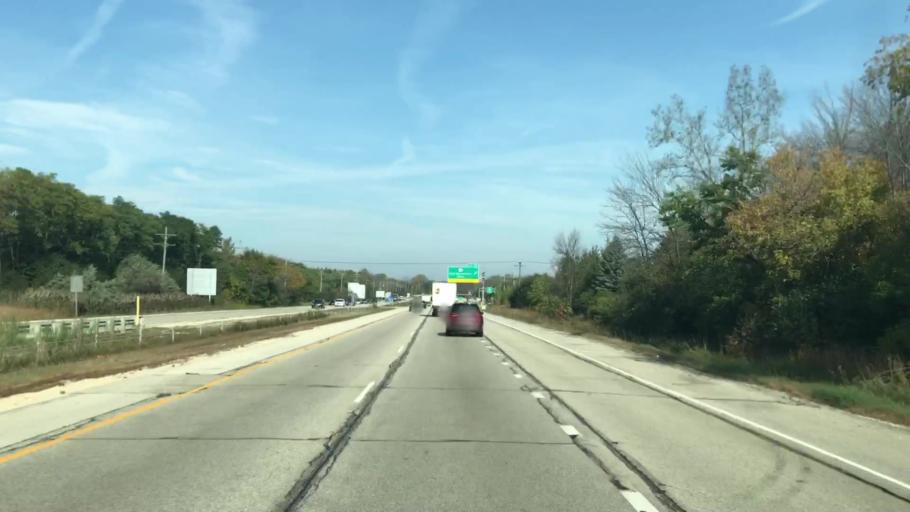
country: US
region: Wisconsin
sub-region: Milwaukee County
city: River Hills
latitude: 43.1825
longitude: -87.9200
